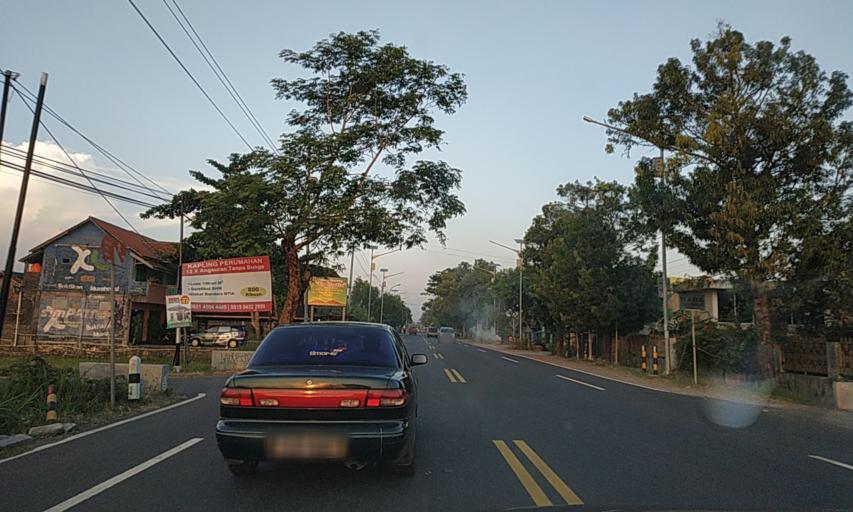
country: ID
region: Daerah Istimewa Yogyakarta
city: Srandakan
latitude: -7.8915
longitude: 110.1237
